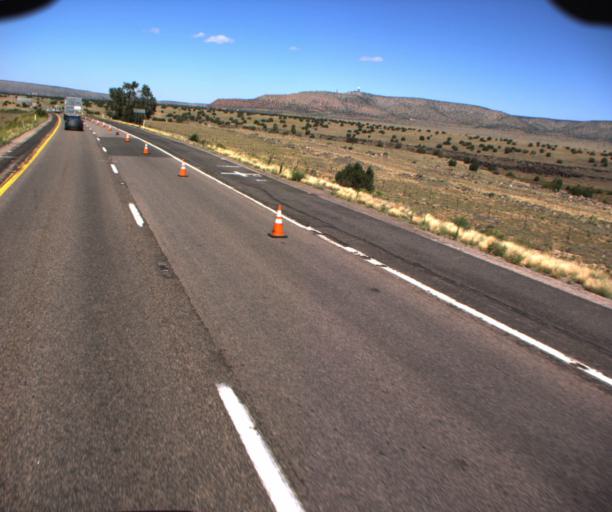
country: US
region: Arizona
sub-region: Mohave County
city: Peach Springs
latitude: 35.3215
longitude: -112.8991
